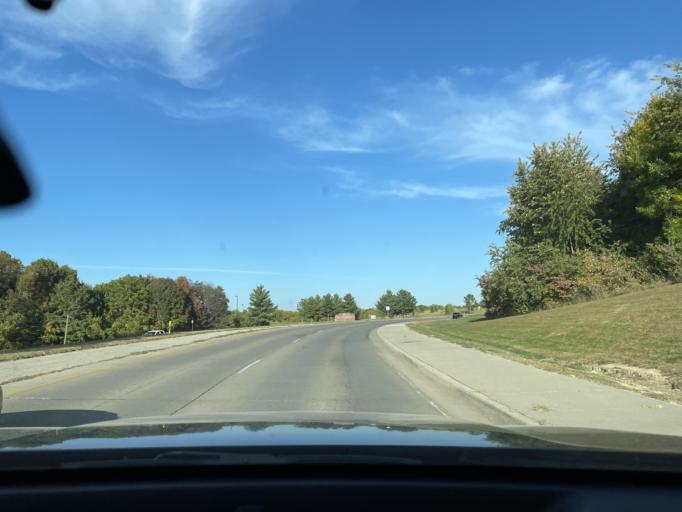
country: US
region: Missouri
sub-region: Buchanan County
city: Saint Joseph
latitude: 39.7691
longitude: -94.8136
